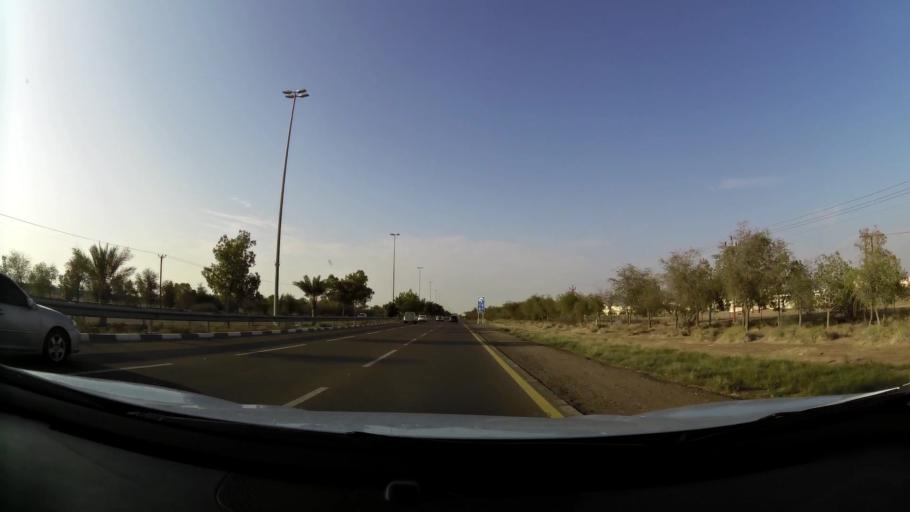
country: AE
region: Abu Dhabi
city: Al Ain
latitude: 24.1007
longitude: 55.8282
